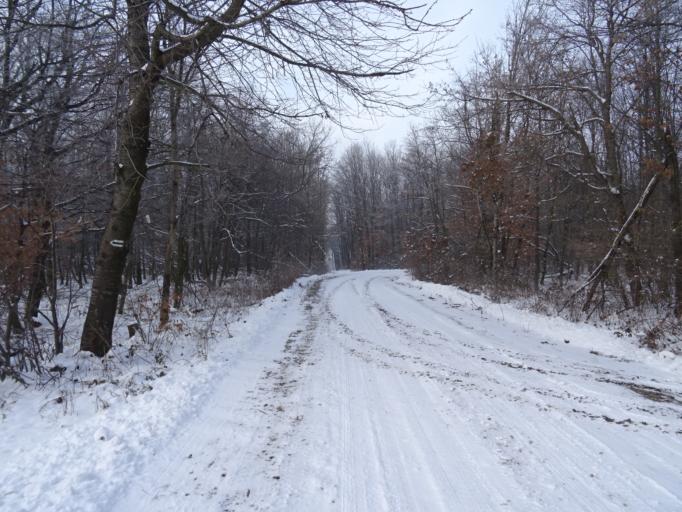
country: HU
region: Fejer
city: Bodajk
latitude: 47.3763
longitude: 18.2729
